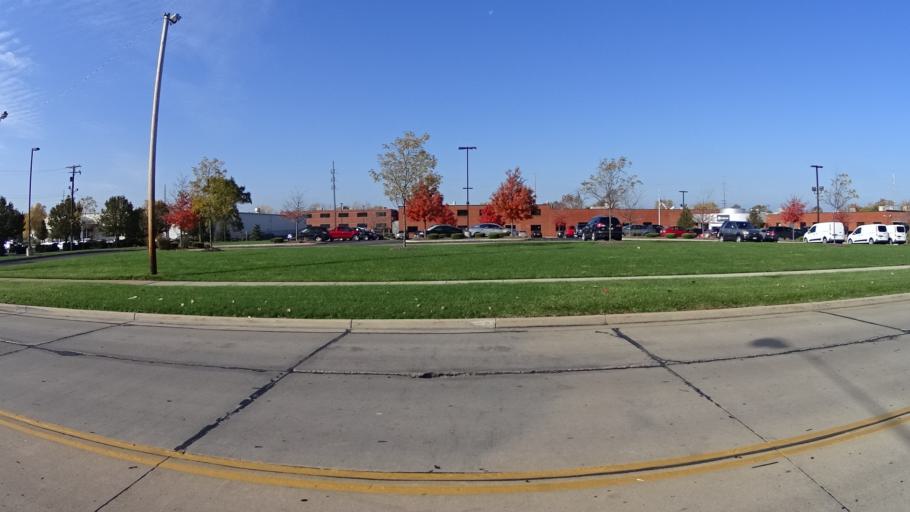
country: US
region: Ohio
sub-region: Lorain County
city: Lorain
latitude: 41.4679
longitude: -82.1568
